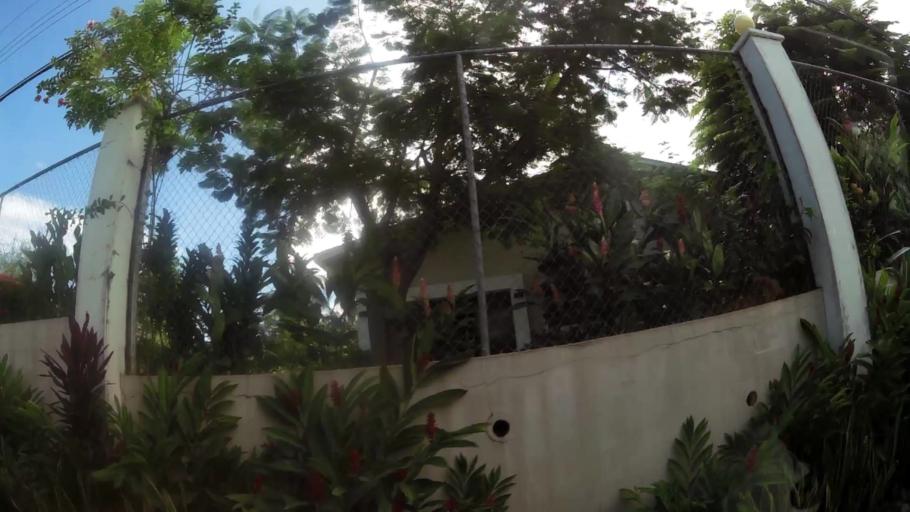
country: PA
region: Panama
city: Nueva Gorgona
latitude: 8.5433
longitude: -79.8800
